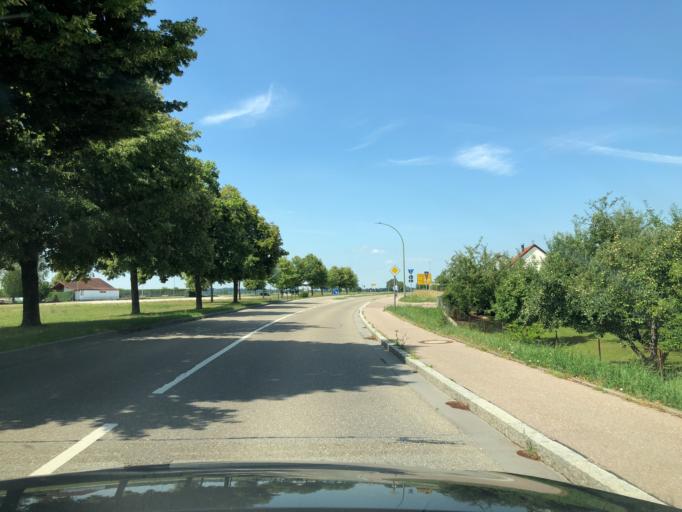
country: DE
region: Bavaria
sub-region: Swabia
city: Oberndorf
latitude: 48.6657
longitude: 10.8712
